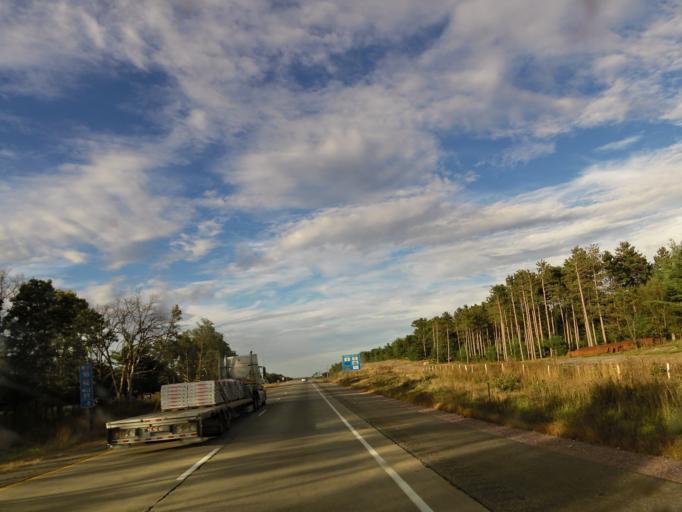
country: US
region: Wisconsin
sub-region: Sauk County
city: Lake Delton
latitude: 43.6006
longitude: -89.8116
